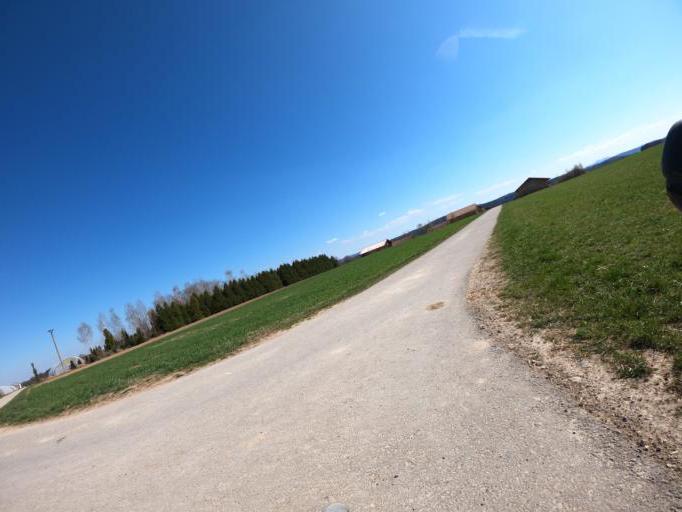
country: DE
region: Baden-Wuerttemberg
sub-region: Tuebingen Region
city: Haigerloch
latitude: 48.3894
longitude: 8.8359
